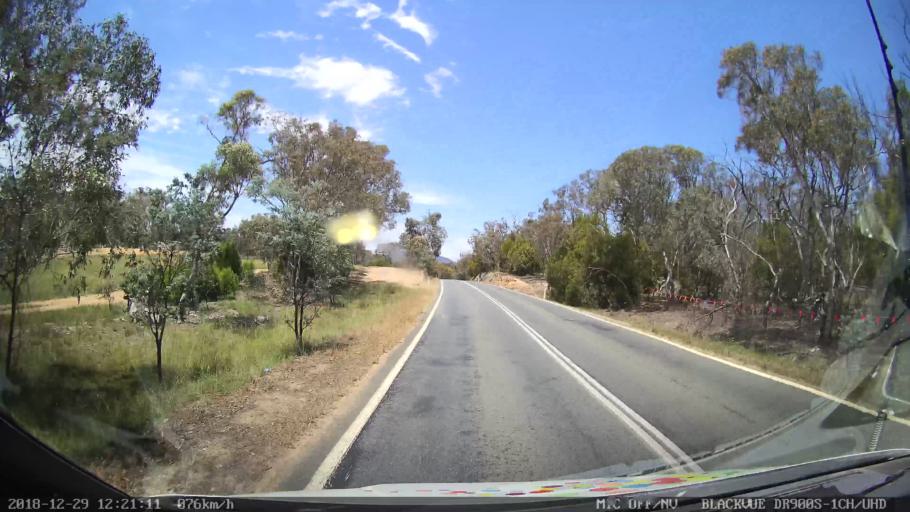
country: AU
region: New South Wales
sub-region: Queanbeyan
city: Queanbeyan
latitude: -35.4107
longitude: 149.2249
